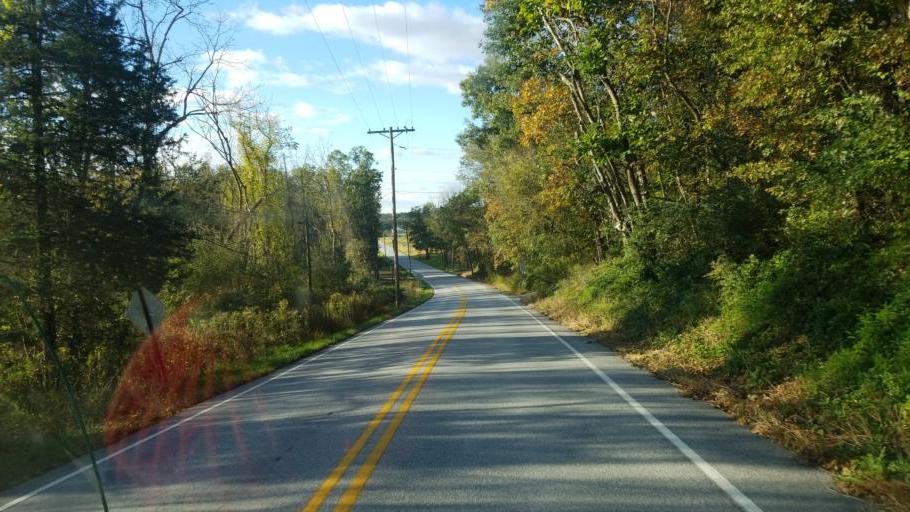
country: US
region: Pennsylvania
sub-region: Adams County
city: Biglerville
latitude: 39.8862
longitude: -77.2285
